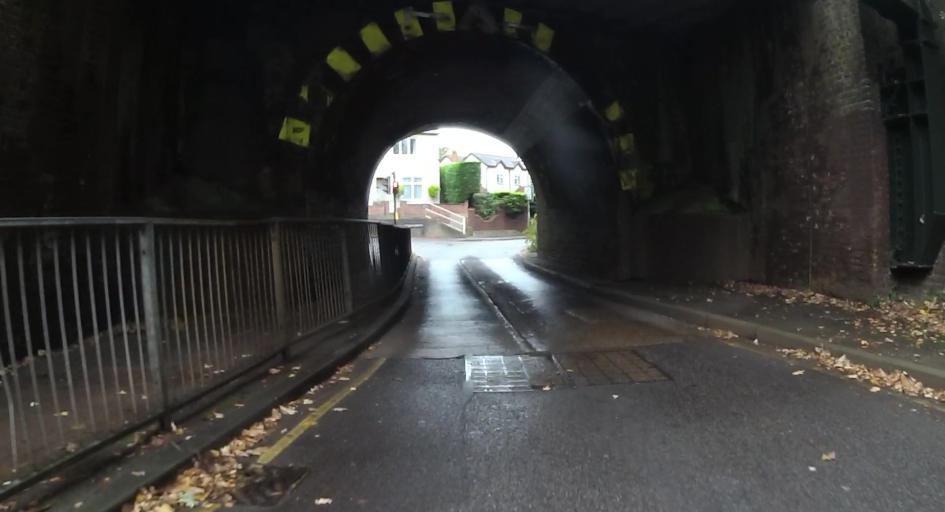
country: GB
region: England
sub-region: Surrey
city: West Byfleet
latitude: 51.3416
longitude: -0.5000
